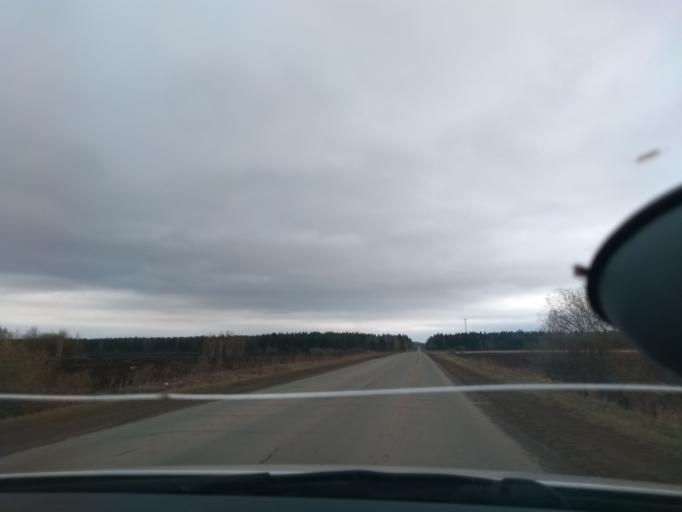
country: RU
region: Perm
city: Kungur
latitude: 57.3908
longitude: 56.8672
